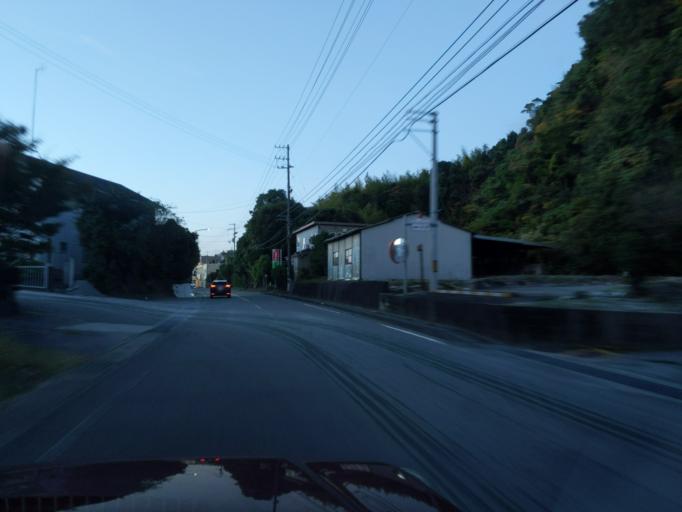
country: JP
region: Tokushima
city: Anan
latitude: 33.8678
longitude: 134.6327
